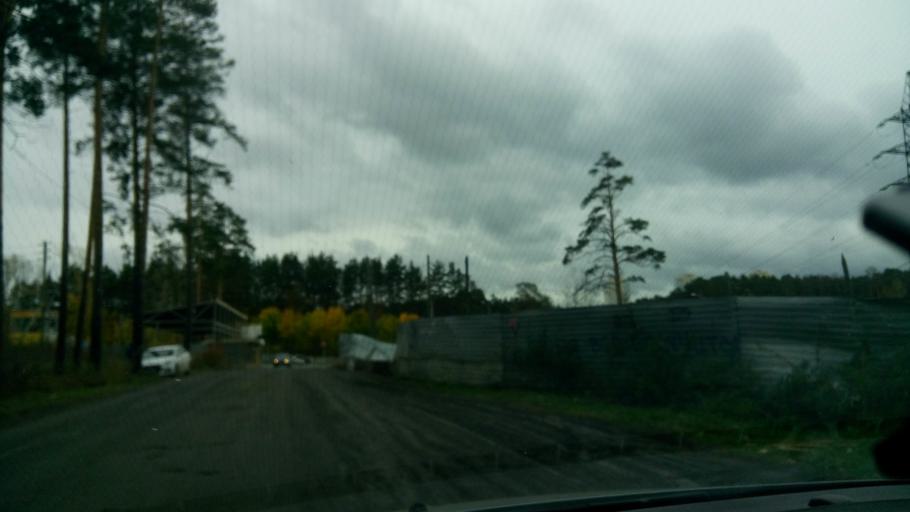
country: RU
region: Sverdlovsk
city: Shirokaya Rechka
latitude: 56.8170
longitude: 60.5233
